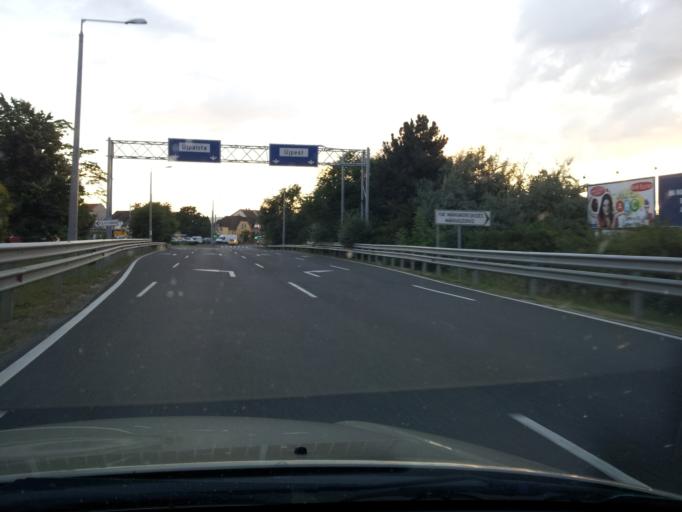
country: HU
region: Budapest
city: Budapest XV. keruelet
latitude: 47.5565
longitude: 19.1292
